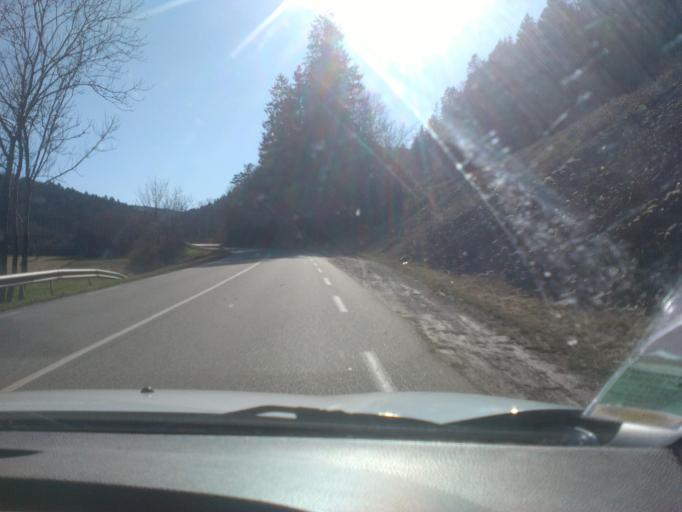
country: FR
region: Alsace
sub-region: Departement du Bas-Rhin
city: Rothau
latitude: 48.4406
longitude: 7.1850
